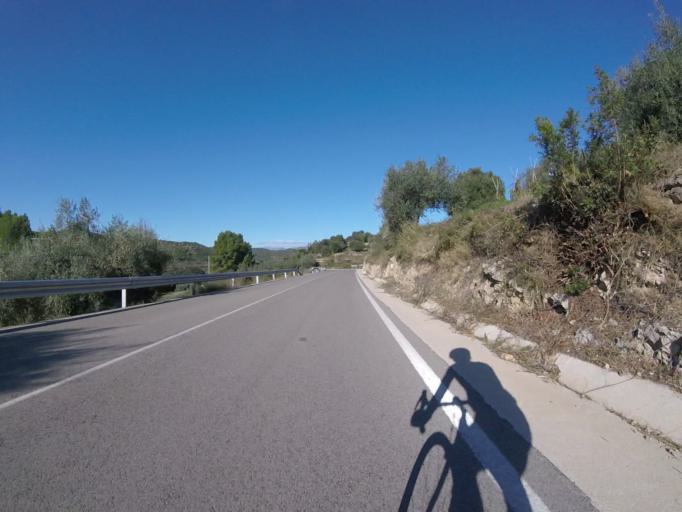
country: ES
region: Valencia
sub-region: Provincia de Castello
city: Cervera del Maestre
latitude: 40.4619
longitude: 0.2585
